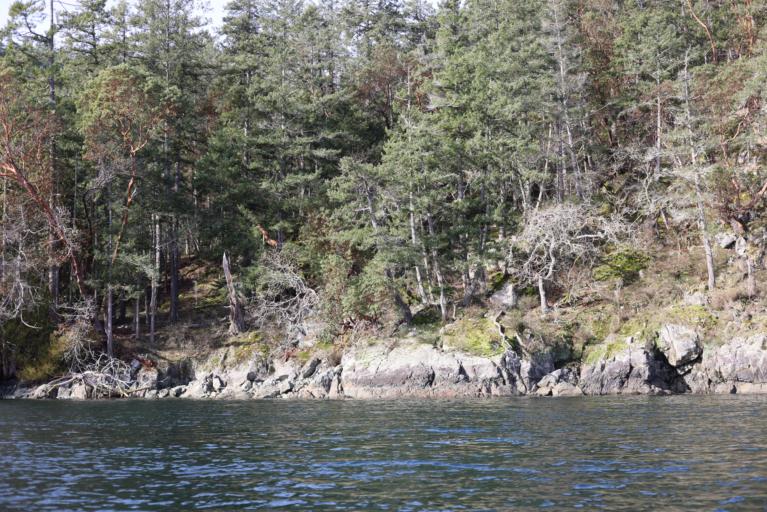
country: CA
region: British Columbia
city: Duncan
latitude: 48.7705
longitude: -123.5768
